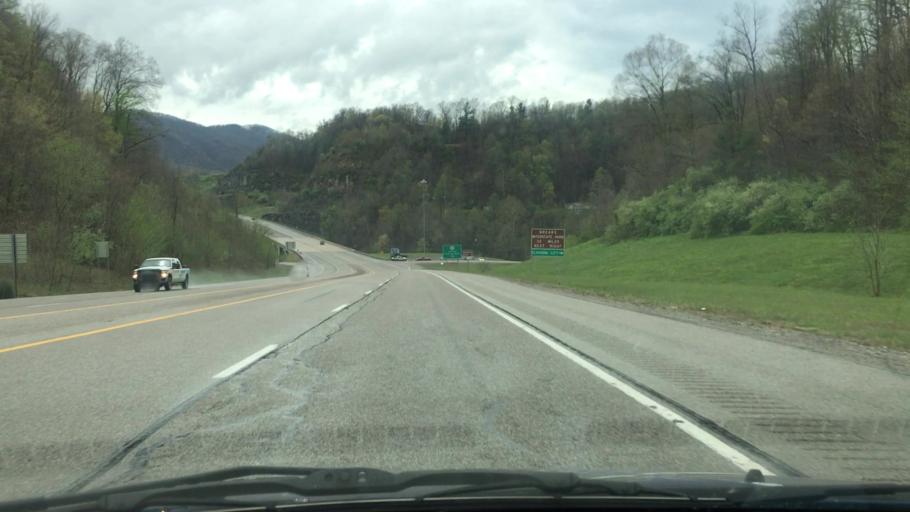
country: US
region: Kentucky
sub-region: Letcher County
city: Jenkins
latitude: 37.1798
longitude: -82.6387
